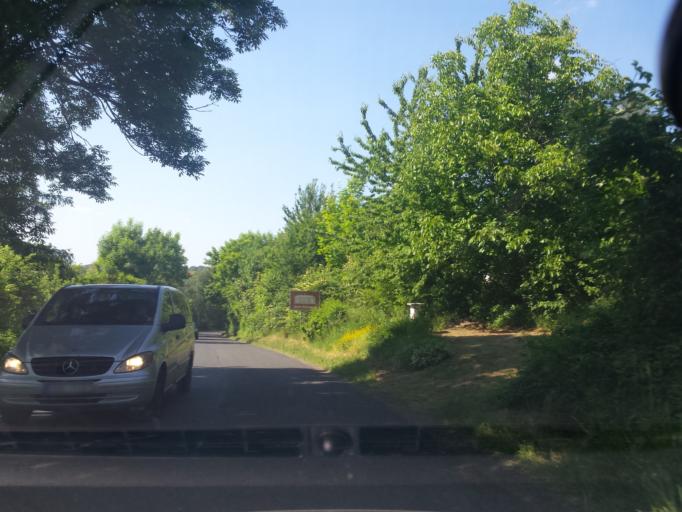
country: CZ
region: Central Bohemia
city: Nelahozeves
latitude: 50.2576
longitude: 14.2970
